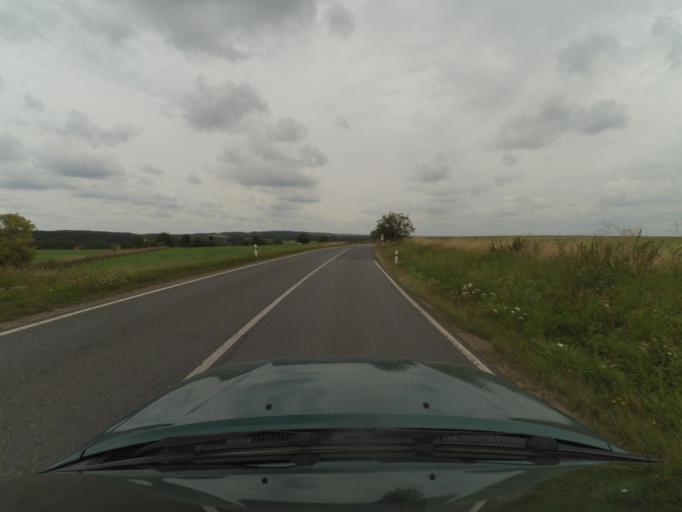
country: CZ
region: Plzensky
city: Kozlany
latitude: 50.0365
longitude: 13.6054
